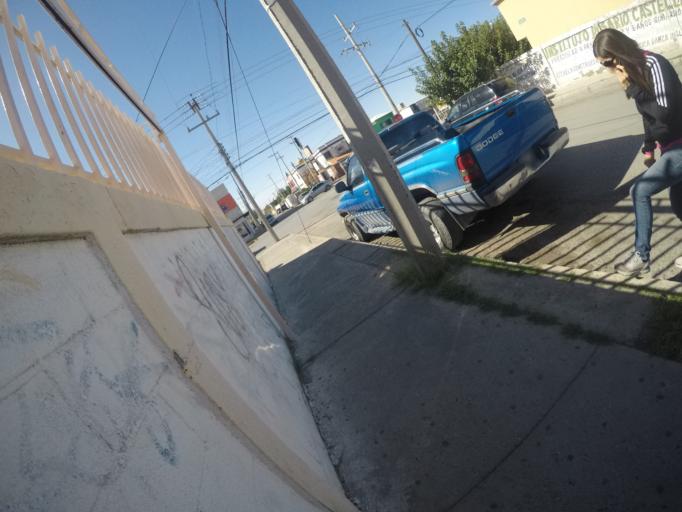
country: US
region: Texas
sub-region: El Paso County
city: Socorro
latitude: 31.6675
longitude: -106.4046
